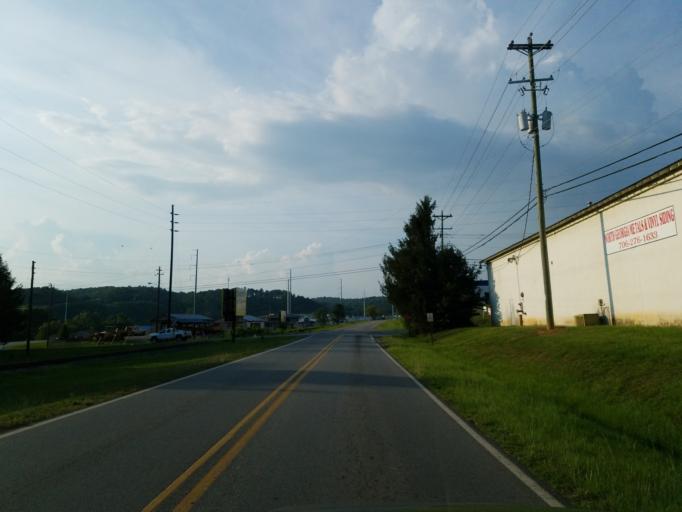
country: US
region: Georgia
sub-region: Gilmer County
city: Ellijay
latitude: 34.6789
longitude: -84.4897
